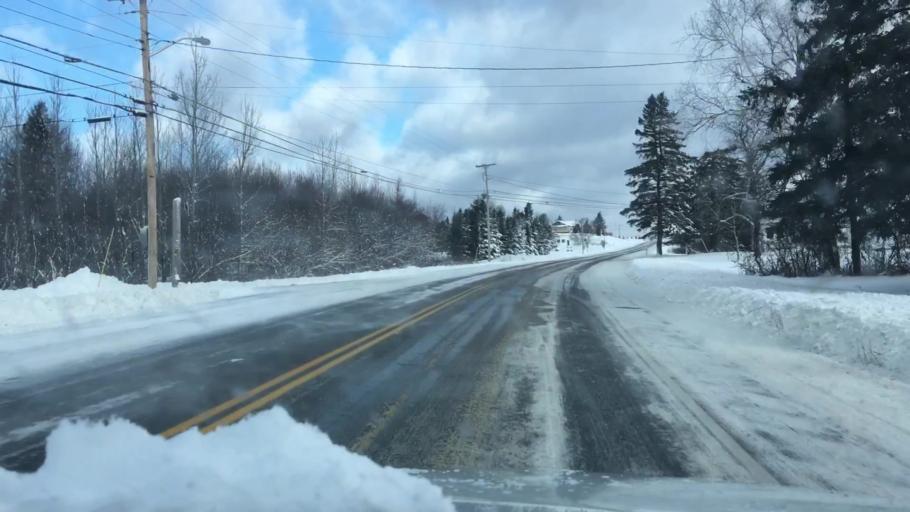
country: US
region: Maine
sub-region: Aroostook County
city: Caribou
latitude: 46.9308
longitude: -68.0234
